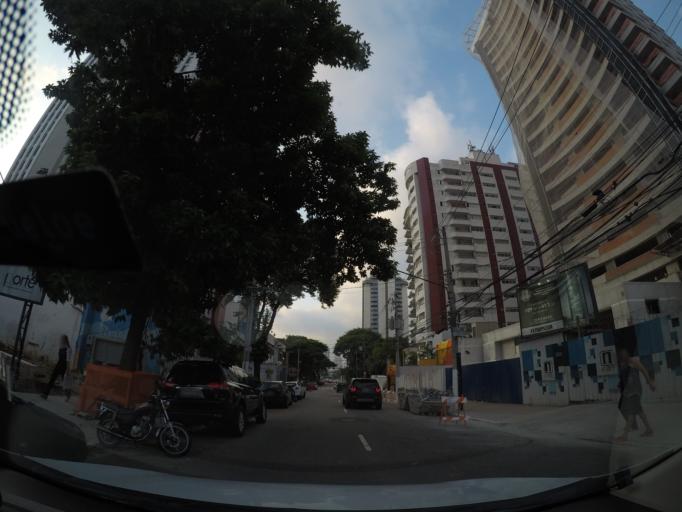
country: BR
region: Sao Paulo
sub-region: Sao Paulo
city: Sao Paulo
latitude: -23.5414
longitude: -46.5672
